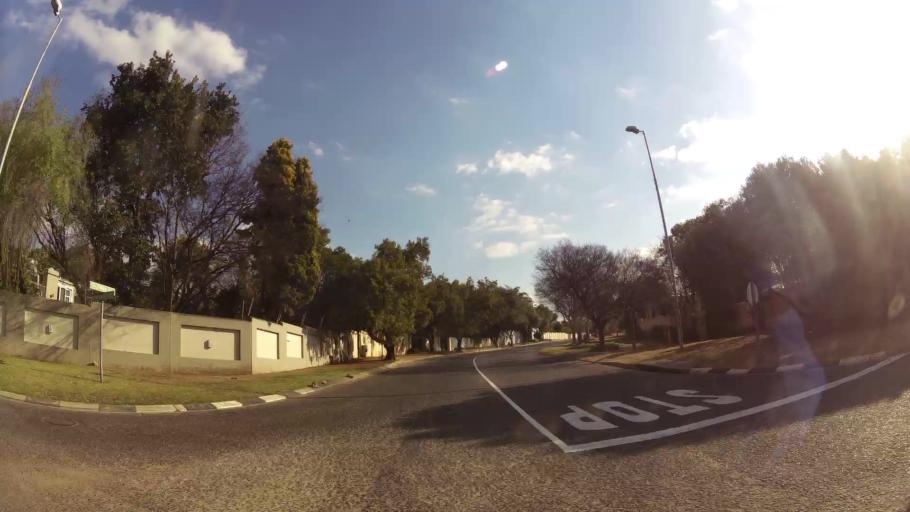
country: ZA
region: Gauteng
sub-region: City of Johannesburg Metropolitan Municipality
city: Diepsloot
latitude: -26.0073
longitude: 28.0284
